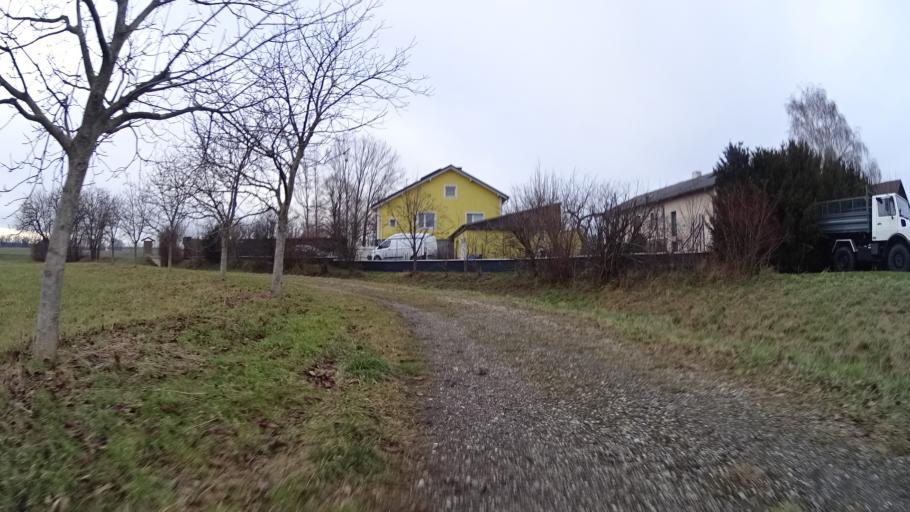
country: AT
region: Lower Austria
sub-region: Politischer Bezirk Korneuburg
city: Harmannsdorf
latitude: 48.3885
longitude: 16.3656
